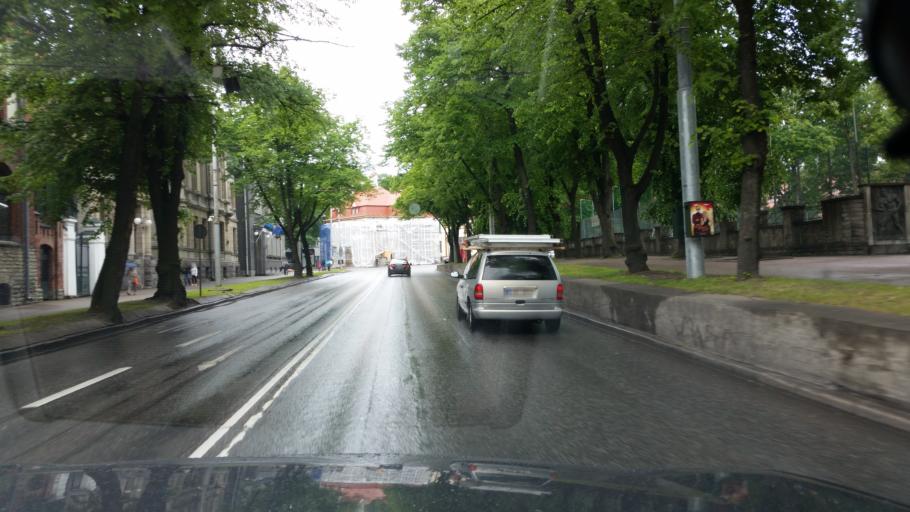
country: EE
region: Harju
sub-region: Tallinna linn
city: Tallinn
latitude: 59.4337
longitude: 24.7496
